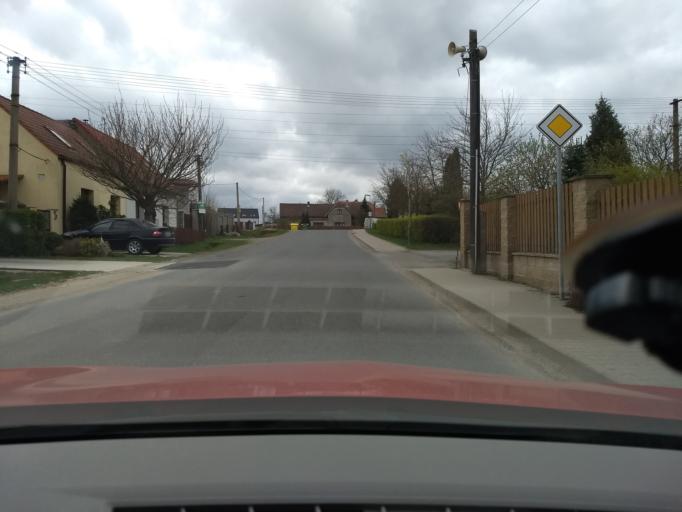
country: CZ
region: Central Bohemia
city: Unhost'
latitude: 50.0675
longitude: 14.1656
